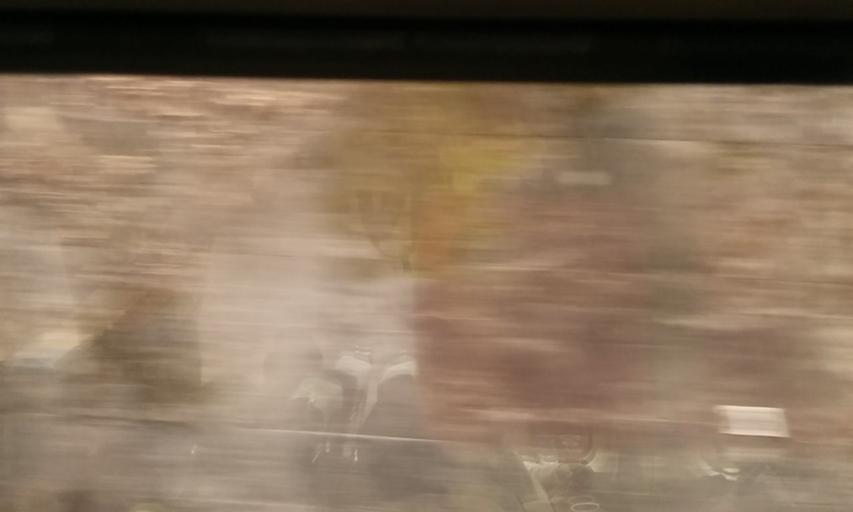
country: JP
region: Nagano
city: Iida
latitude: 35.7453
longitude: 137.7156
